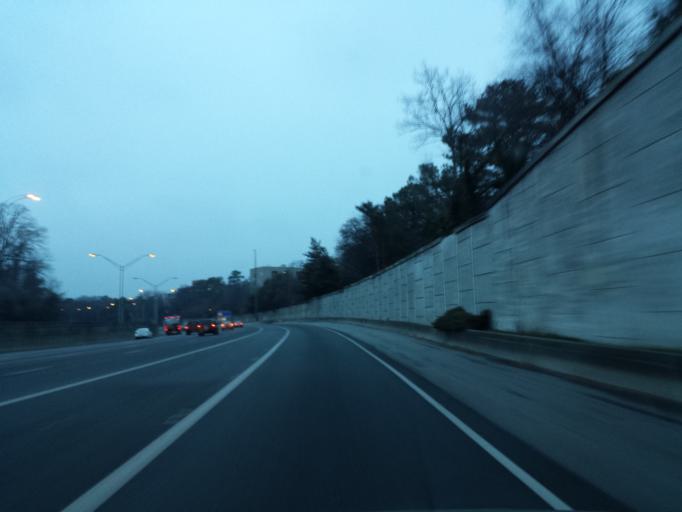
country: US
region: Georgia
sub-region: Fulton County
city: Atlanta
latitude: 33.7989
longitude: -84.3958
